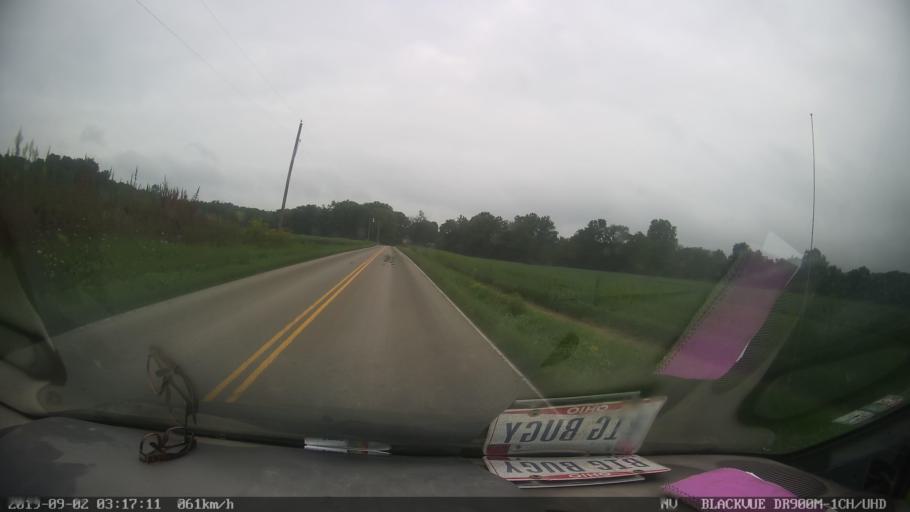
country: US
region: Ohio
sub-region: Knox County
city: Fredericktown
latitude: 40.5401
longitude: -82.6263
